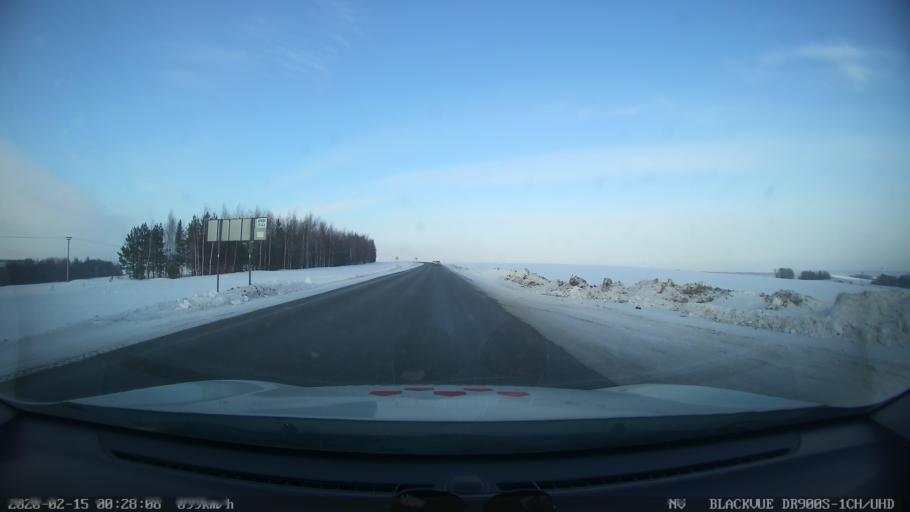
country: RU
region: Tatarstan
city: Verkhniy Uslon
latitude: 55.6380
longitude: 48.8739
